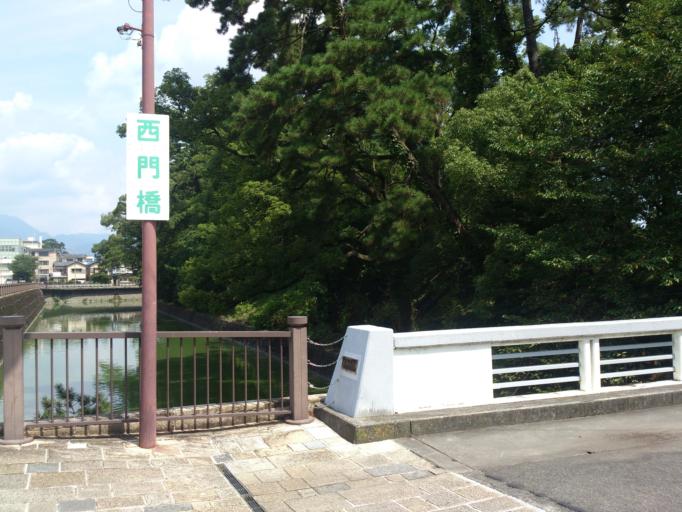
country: JP
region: Shizuoka
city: Shizuoka-shi
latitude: 34.9798
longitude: 138.3810
